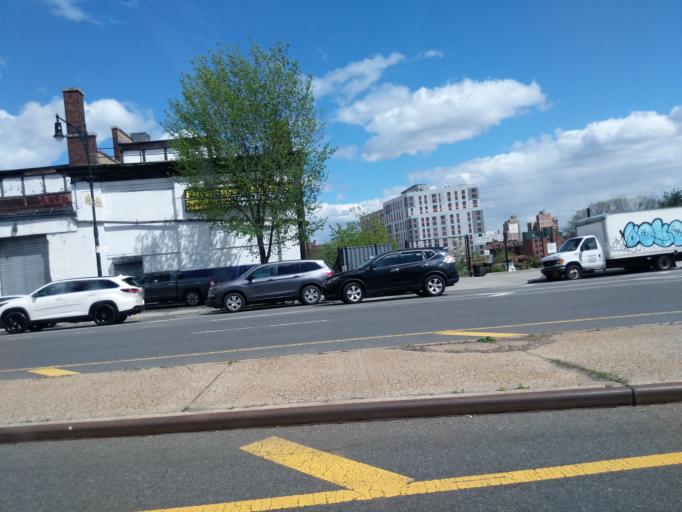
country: US
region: New York
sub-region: New York County
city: Inwood
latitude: 40.8216
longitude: -73.9254
